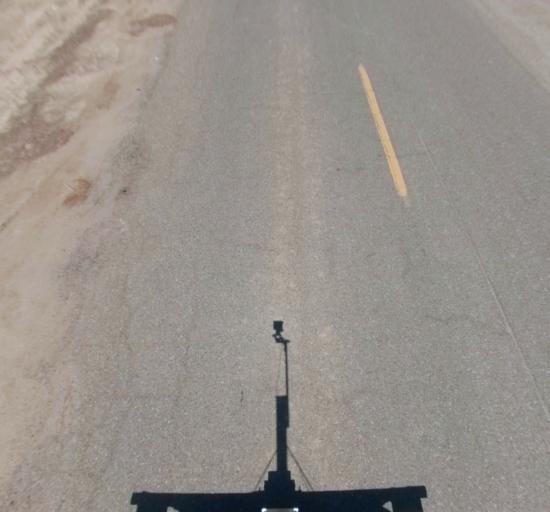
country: US
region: California
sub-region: Madera County
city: Chowchilla
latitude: 37.0887
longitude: -120.2837
